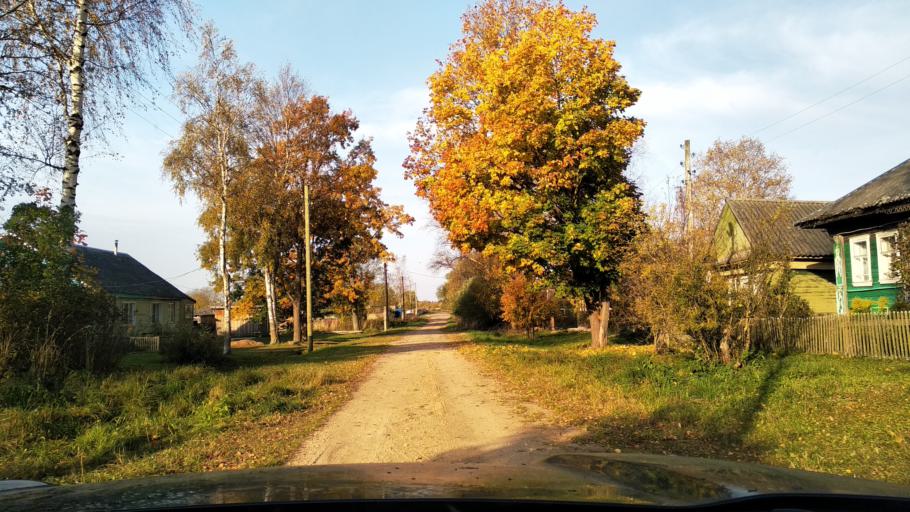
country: RU
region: Tverskaya
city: Krasnyy Kholm
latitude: 58.0094
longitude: 37.1877
